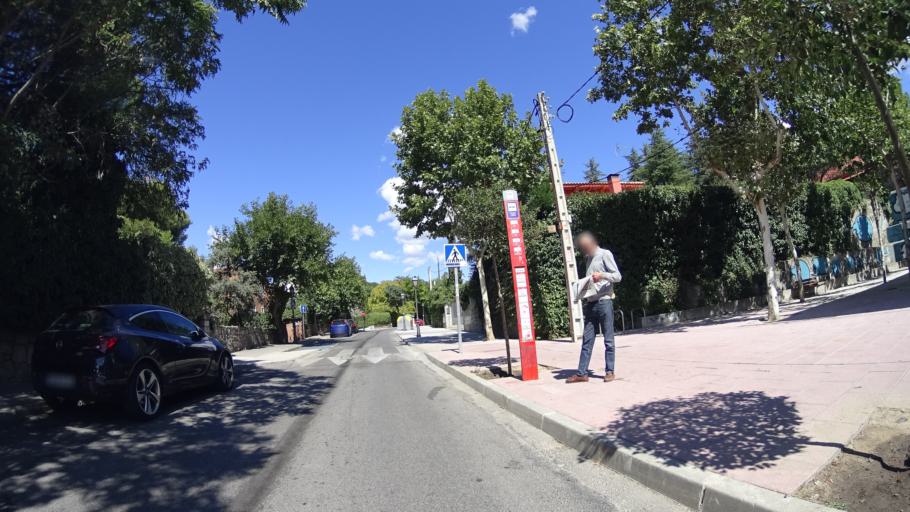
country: ES
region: Madrid
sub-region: Provincia de Madrid
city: Torrelodones
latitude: 40.5769
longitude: -3.9541
